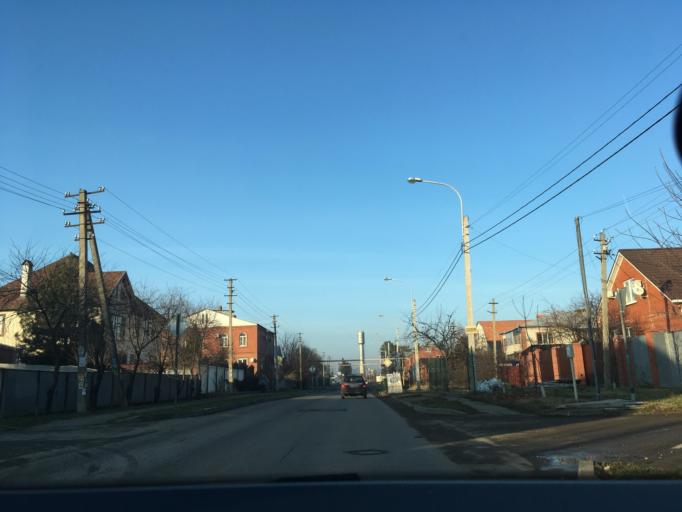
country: RU
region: Krasnodarskiy
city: Krasnodar
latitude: 45.1239
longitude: 39.0140
